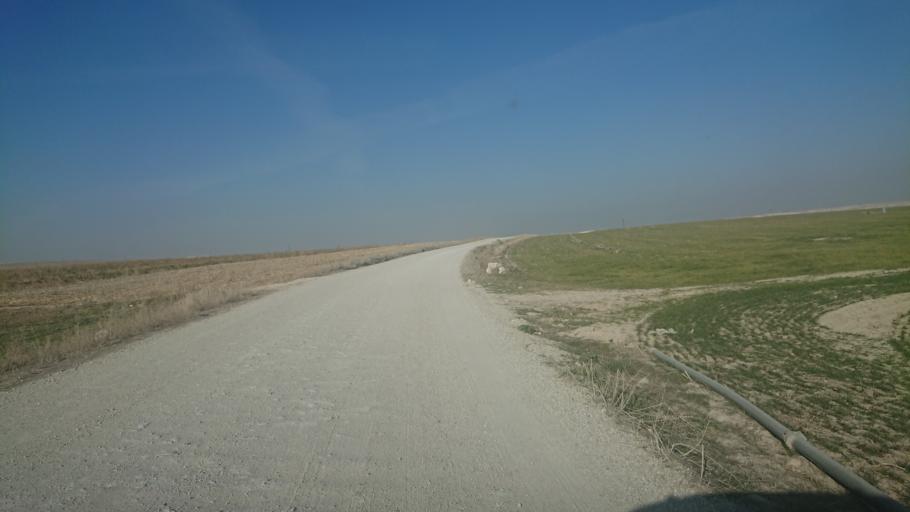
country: TR
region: Aksaray
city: Sultanhani
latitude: 38.0418
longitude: 33.6058
